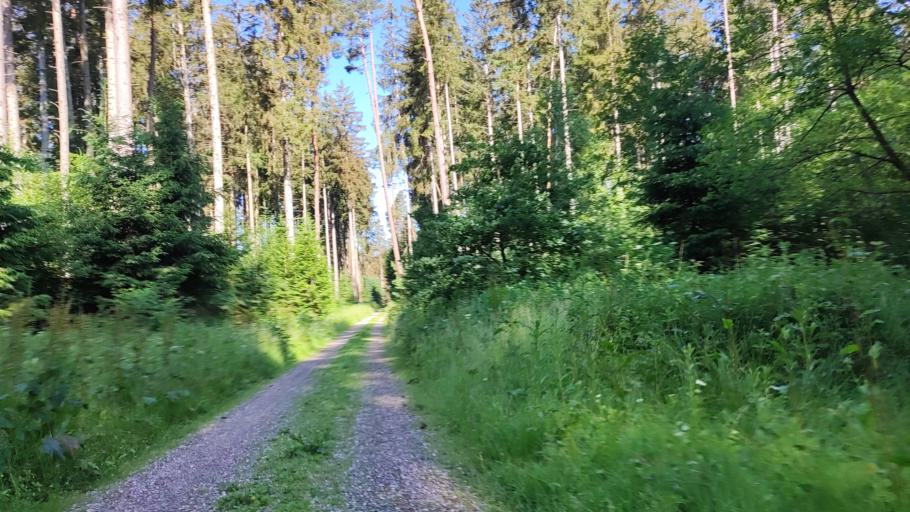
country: DE
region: Bavaria
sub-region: Swabia
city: Horgau
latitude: 48.3796
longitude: 10.7096
